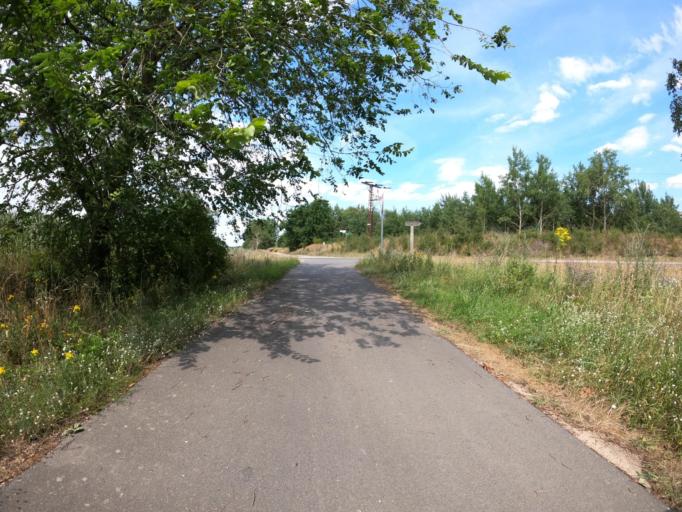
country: DE
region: Mecklenburg-Vorpommern
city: Woldegk
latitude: 53.3418
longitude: 13.5991
